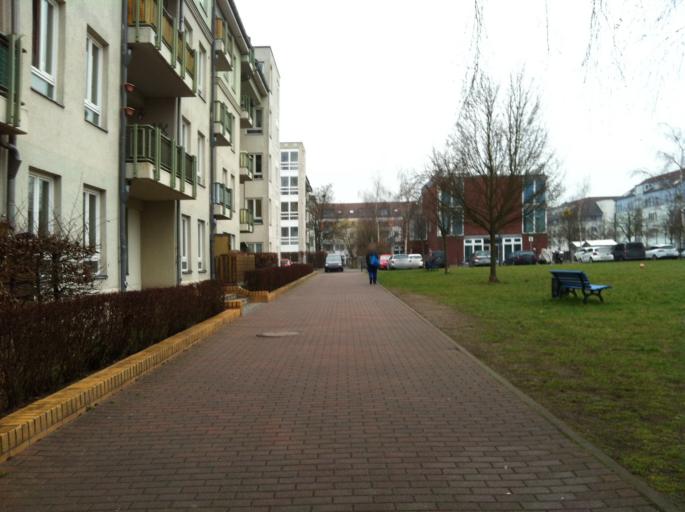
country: DE
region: Berlin
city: Karow
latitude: 52.6150
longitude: 13.4927
